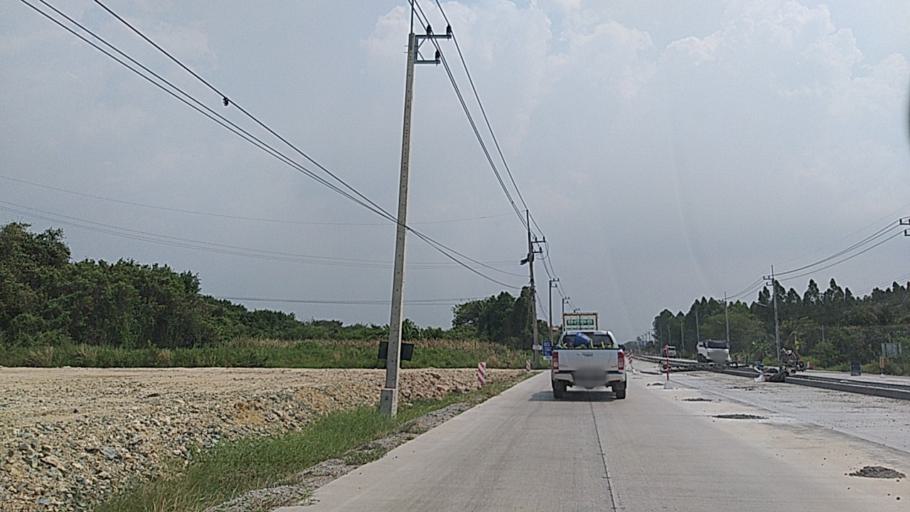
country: TH
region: Chon Buri
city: Phanat Nikhom
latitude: 13.3777
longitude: 101.1945
